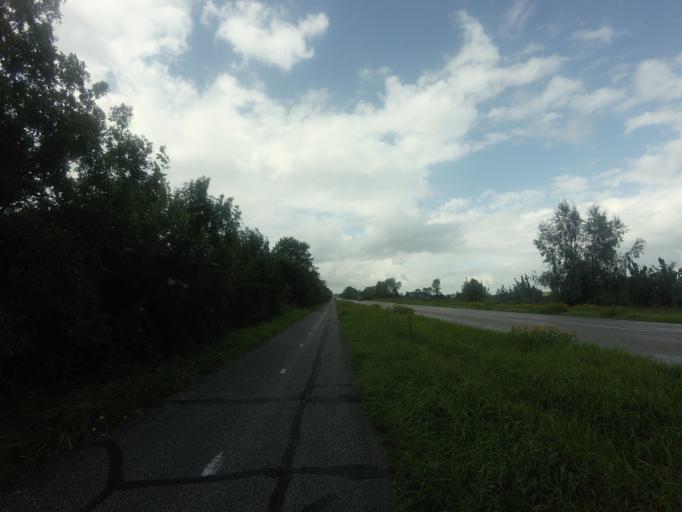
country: NL
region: Friesland
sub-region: Gemeente Skarsterlan
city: Joure
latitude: 52.9705
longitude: 5.7642
